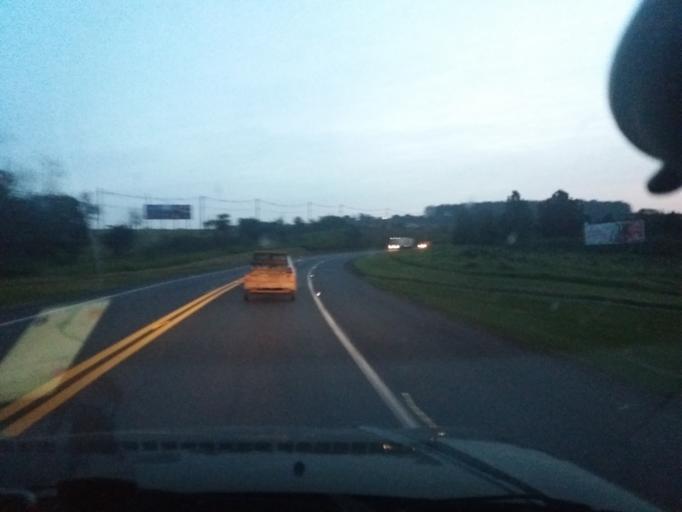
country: BR
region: Sao Paulo
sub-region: Itapeva
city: Itapeva
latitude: -23.9782
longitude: -48.8476
